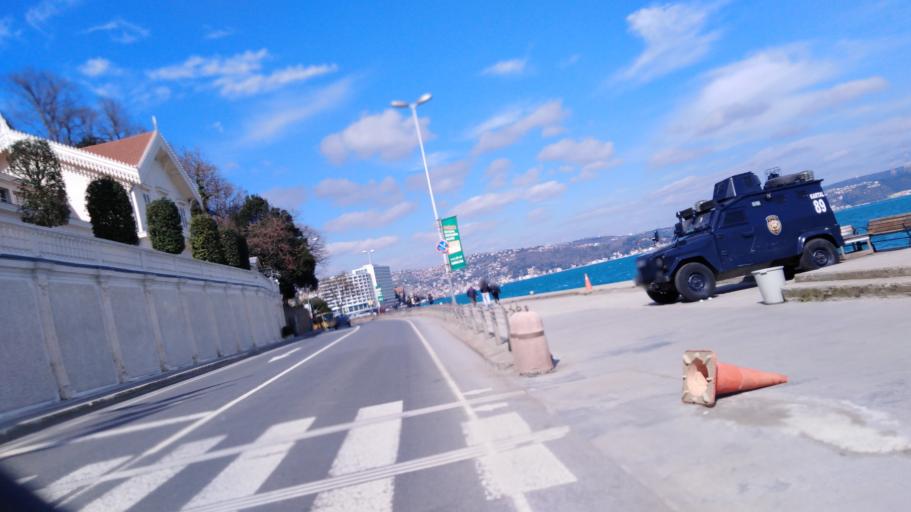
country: TR
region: Istanbul
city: Sisli
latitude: 41.1345
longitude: 29.0621
